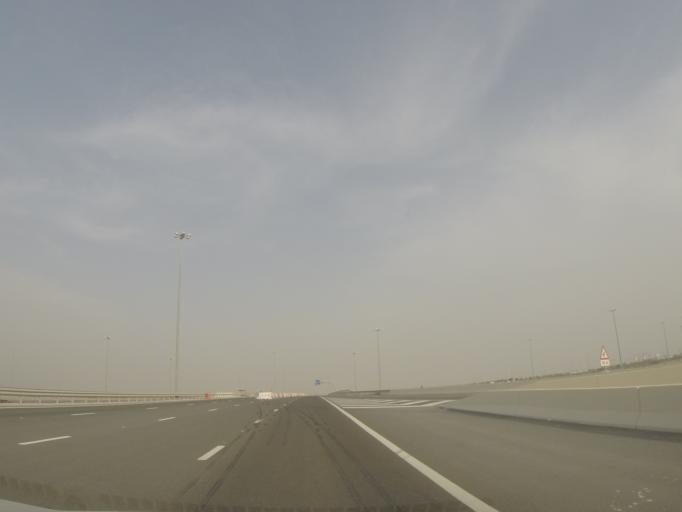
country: AE
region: Abu Dhabi
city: Abu Dhabi
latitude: 24.6953
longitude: 54.7773
